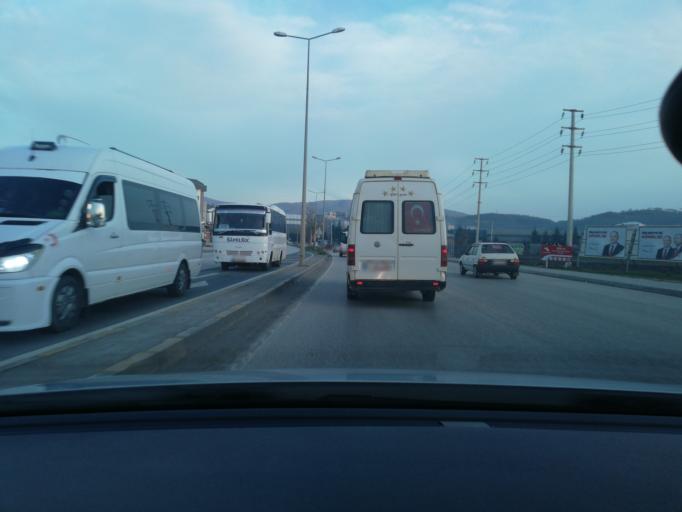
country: TR
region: Duzce
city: Konuralp
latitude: 40.8950
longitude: 31.1668
